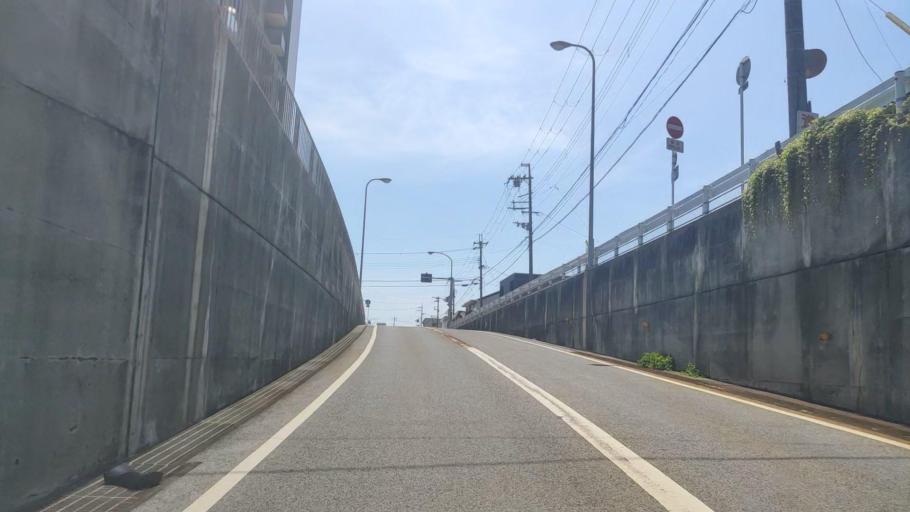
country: JP
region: Shiga Prefecture
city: Nagahama
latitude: 35.3799
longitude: 136.2637
